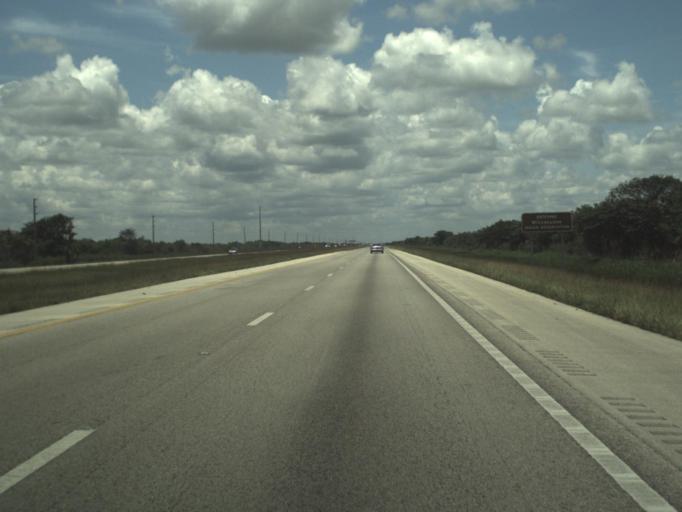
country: US
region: Florida
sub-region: Broward County
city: Weston
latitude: 26.1594
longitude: -80.7817
